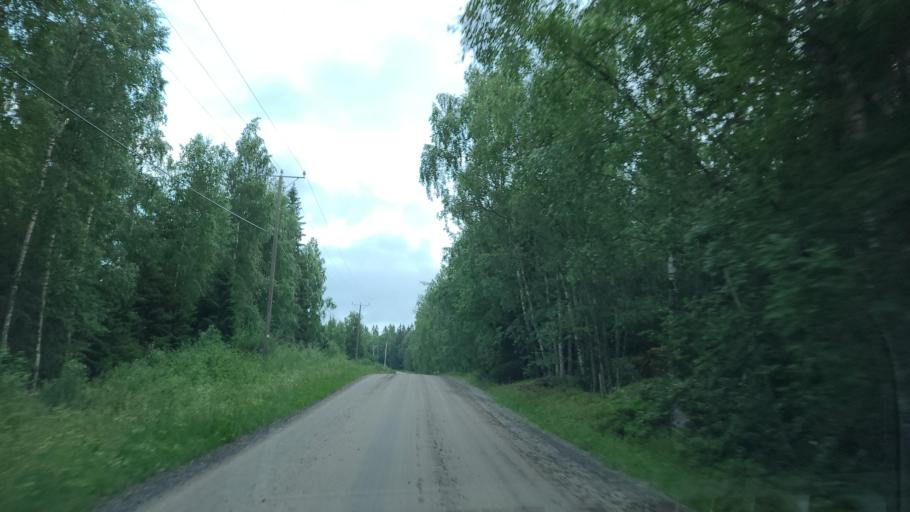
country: FI
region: Ostrobothnia
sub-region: Vaasa
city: Replot
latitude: 63.3083
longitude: 21.1574
